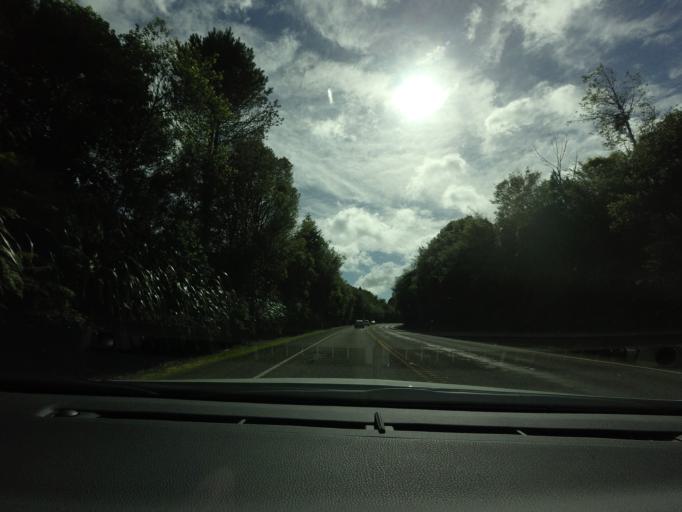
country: NZ
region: Bay of Plenty
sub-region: Rotorua District
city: Rotorua
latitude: -38.0730
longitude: 176.1690
